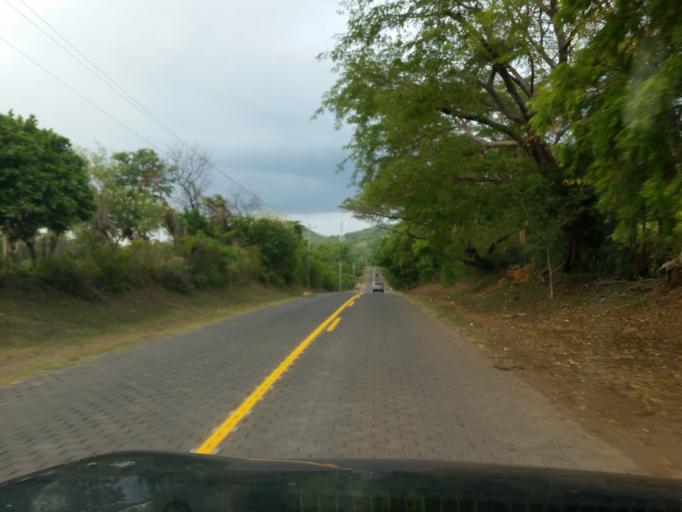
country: NI
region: Managua
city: Masachapa
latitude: 11.8526
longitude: -86.5178
